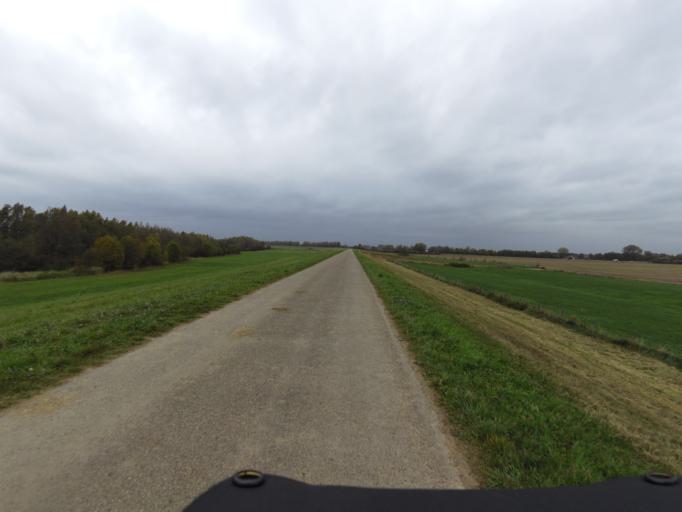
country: NL
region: Gelderland
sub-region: Gemeente Zevenaar
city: Zevenaar
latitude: 51.8680
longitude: 6.1002
